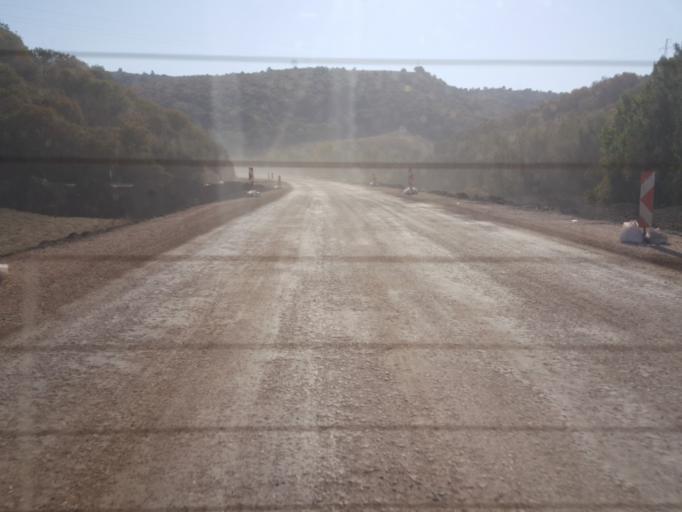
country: TR
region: Corum
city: Seydim
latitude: 40.5692
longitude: 34.7655
